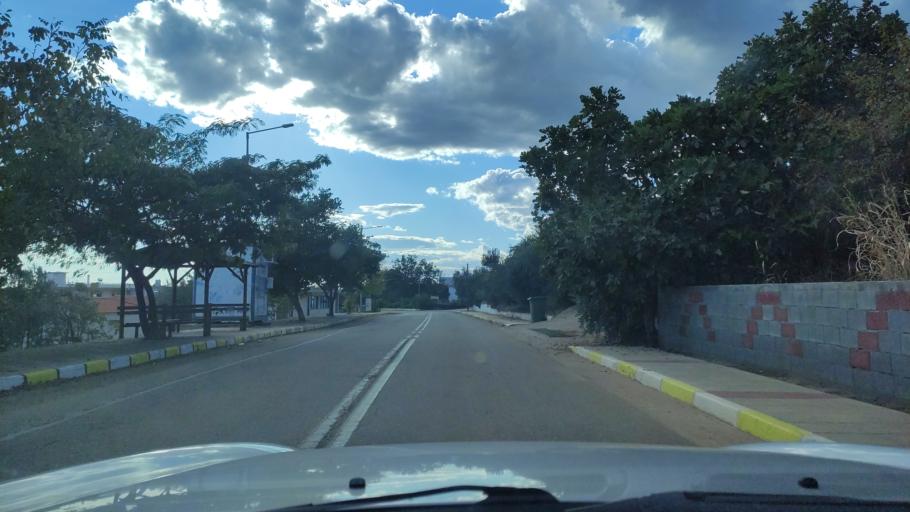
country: GR
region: East Macedonia and Thrace
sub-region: Nomos Rodopis
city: Iasmos
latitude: 41.1195
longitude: 25.1270
